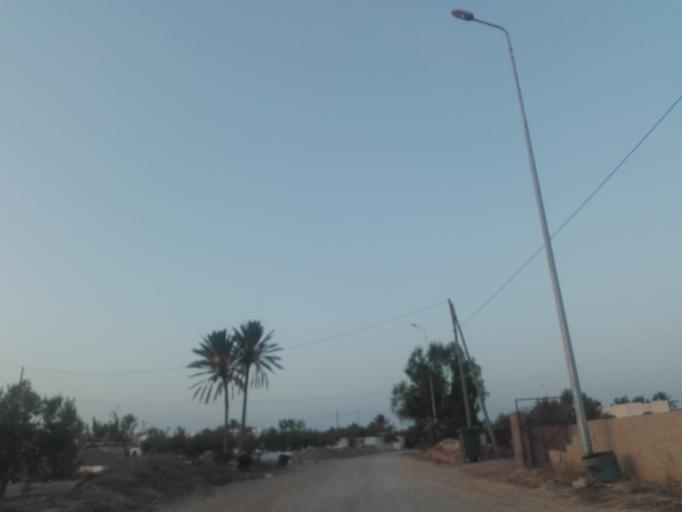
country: TN
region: Madanin
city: Houmt Souk
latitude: 33.7567
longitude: 10.7723
